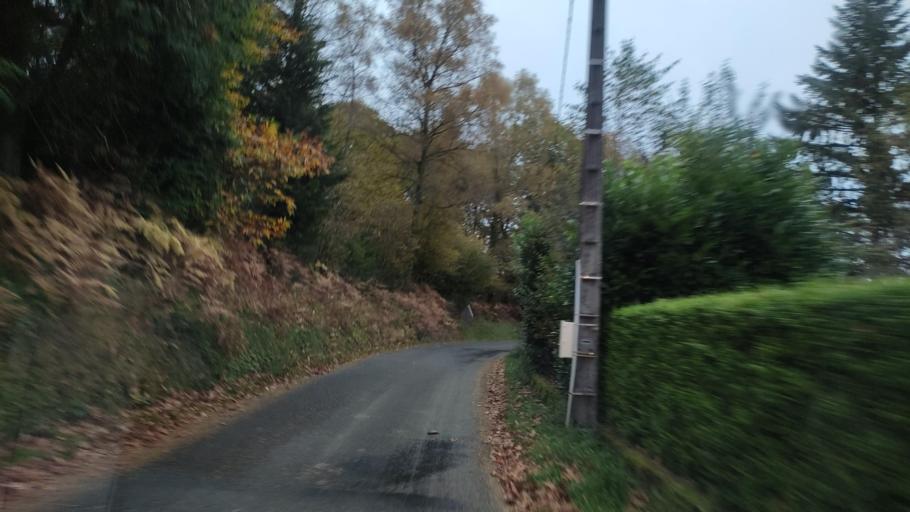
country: FR
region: Limousin
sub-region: Departement de la Haute-Vienne
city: Ambazac
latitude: 46.0146
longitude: 1.4561
